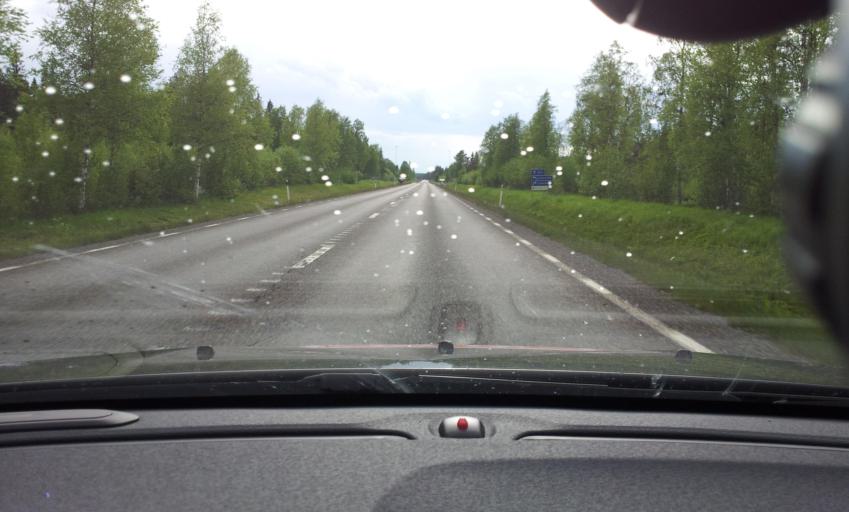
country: SE
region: Jaemtland
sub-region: OEstersunds Kommun
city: Lit
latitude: 63.2045
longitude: 14.8860
